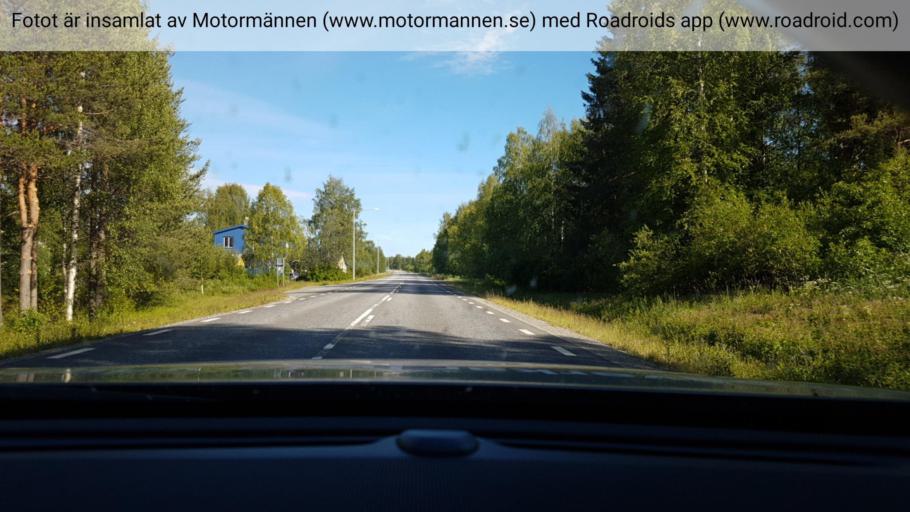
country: SE
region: Vaesterbotten
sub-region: Lycksele Kommun
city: Lycksele
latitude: 64.7005
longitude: 18.3643
